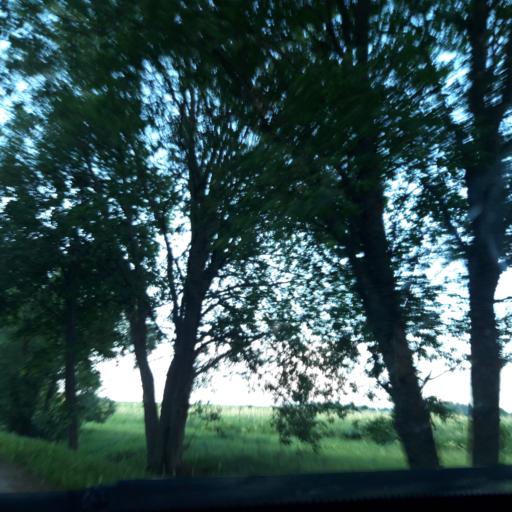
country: LV
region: Talsu Rajons
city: Sabile
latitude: 57.0295
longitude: 22.6103
